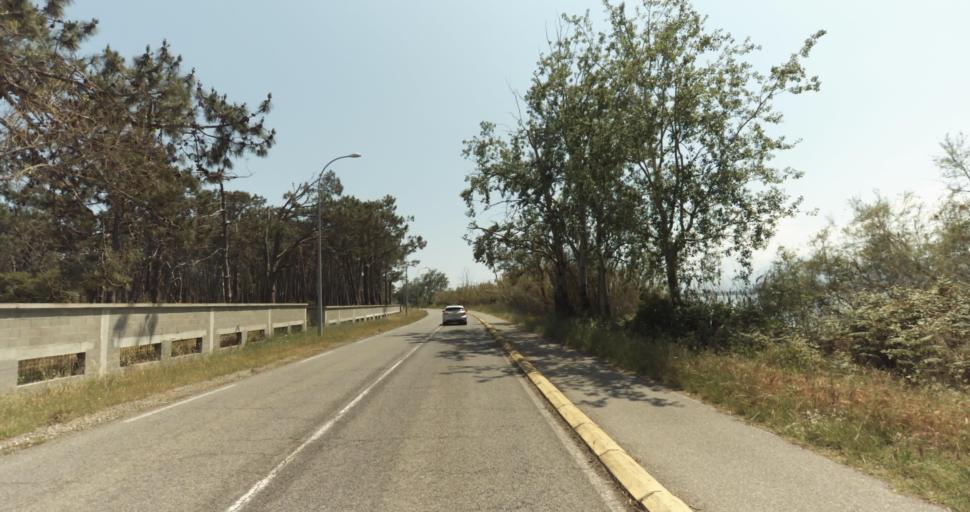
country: FR
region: Corsica
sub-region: Departement de la Haute-Corse
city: Biguglia
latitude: 42.6215
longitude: 9.4738
